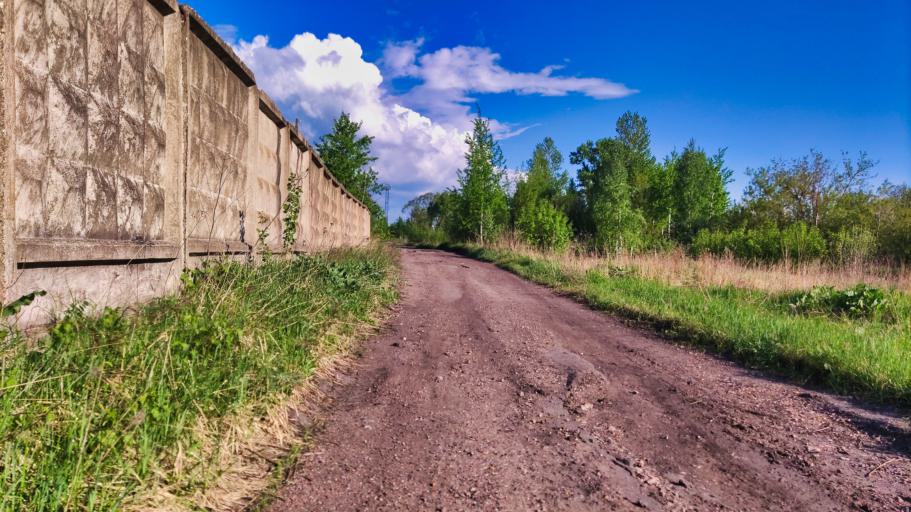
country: RU
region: Tverskaya
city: Rzhev
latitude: 56.2416
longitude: 34.3388
